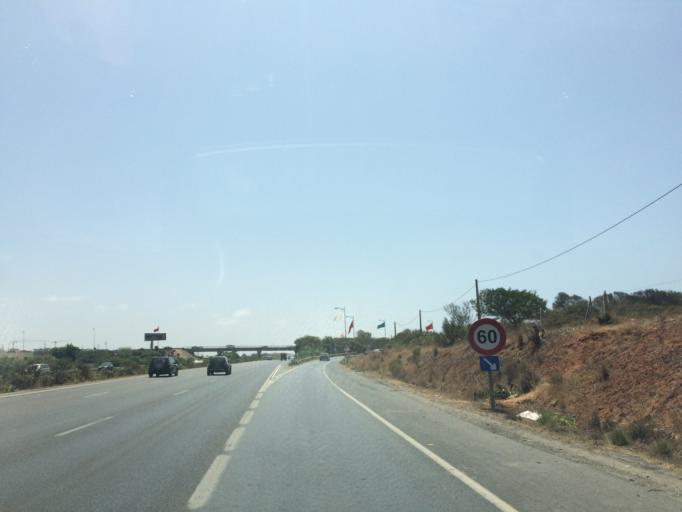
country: MA
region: Rabat-Sale-Zemmour-Zaer
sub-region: Skhirate-Temara
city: Temara
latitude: 33.9352
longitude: -6.9342
